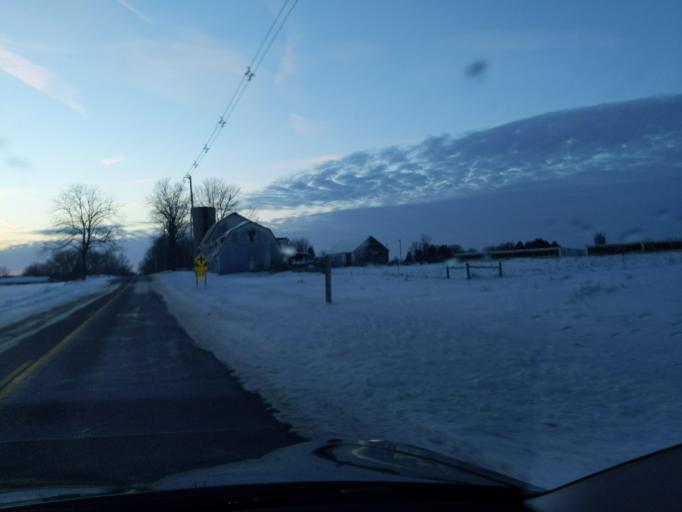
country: US
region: Michigan
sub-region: Ingham County
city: Mason
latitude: 42.5820
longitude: -84.3812
